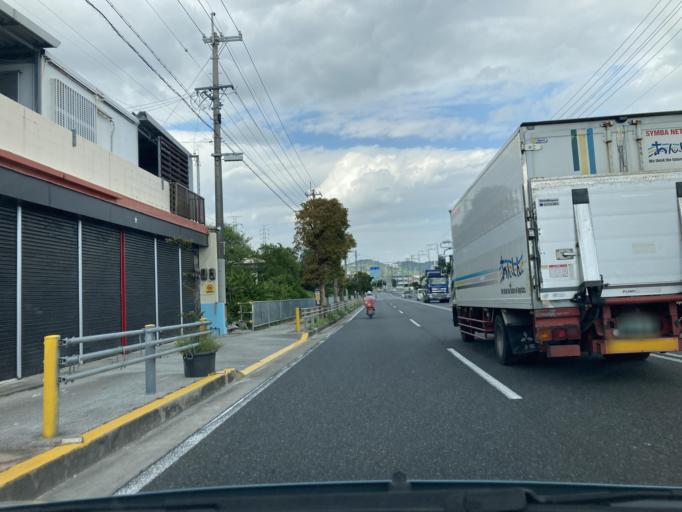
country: JP
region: Okinawa
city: Ginowan
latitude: 26.2517
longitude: 127.7832
